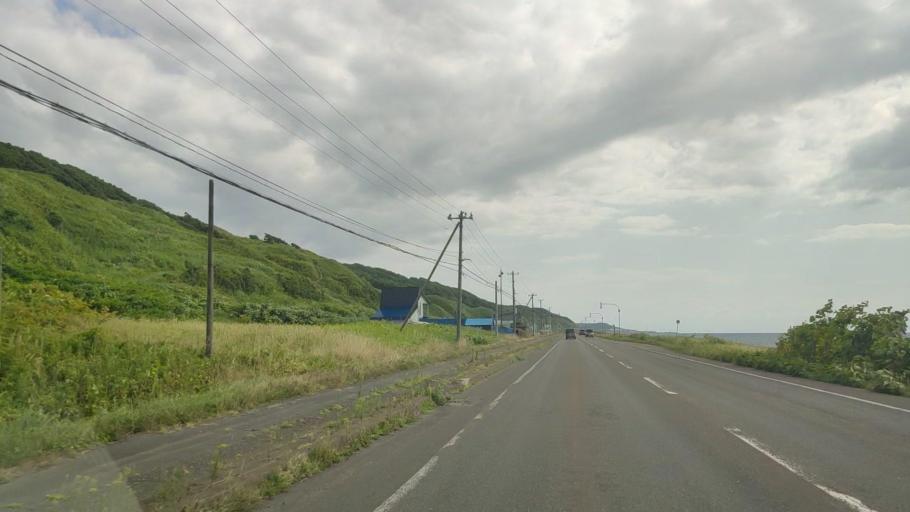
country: JP
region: Hokkaido
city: Rumoi
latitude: 44.1907
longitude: 141.6585
